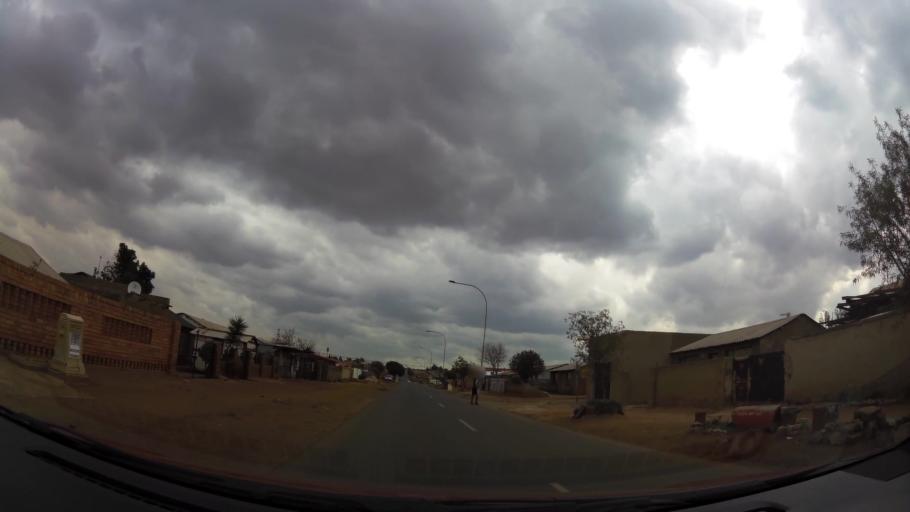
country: ZA
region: Gauteng
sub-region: City of Johannesburg Metropolitan Municipality
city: Soweto
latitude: -26.2596
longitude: 27.8413
